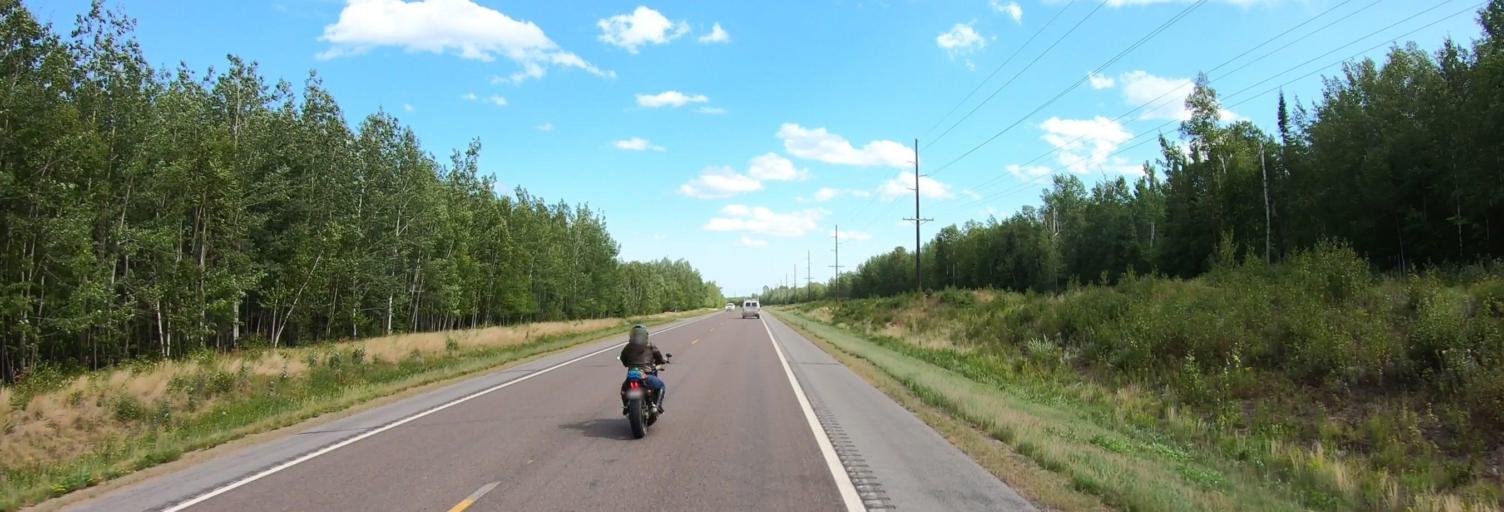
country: US
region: Minnesota
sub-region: Saint Louis County
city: Virginia
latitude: 47.8566
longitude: -92.4292
